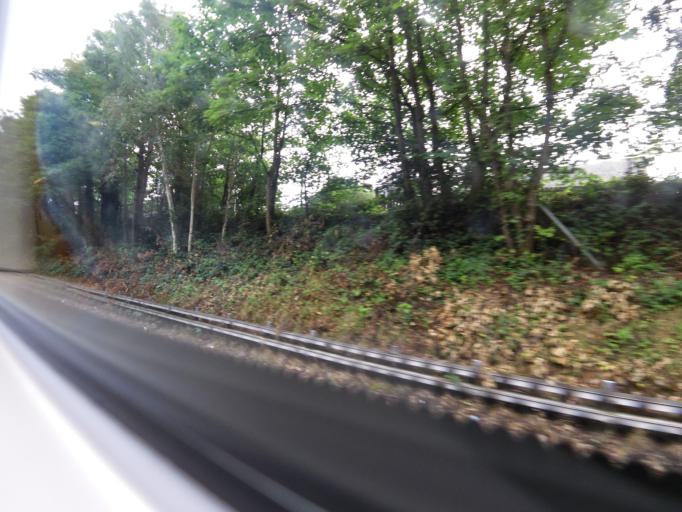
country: GB
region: England
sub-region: Greater London
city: Croydon
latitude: 51.3849
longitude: -0.0922
